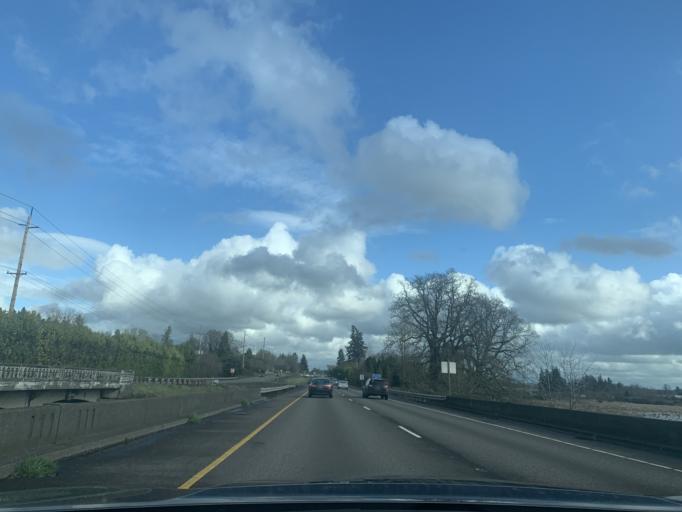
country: US
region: Oregon
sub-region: Washington County
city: Sherwood
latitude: 45.3815
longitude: -122.8271
